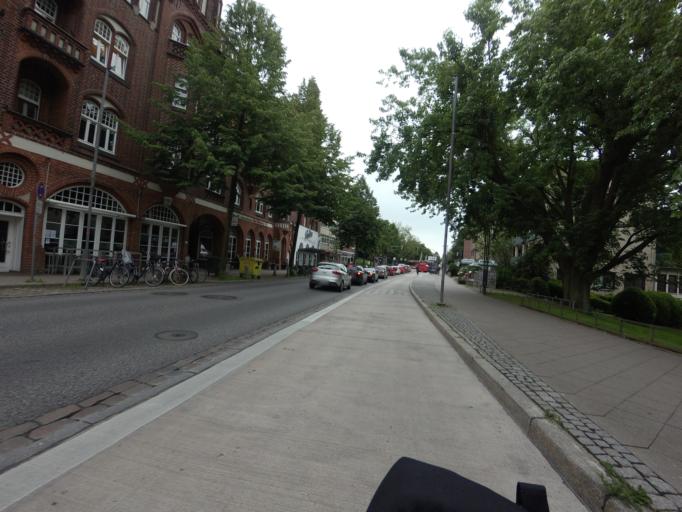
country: DE
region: Schleswig-Holstein
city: Luebeck
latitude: 53.8606
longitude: 10.6898
